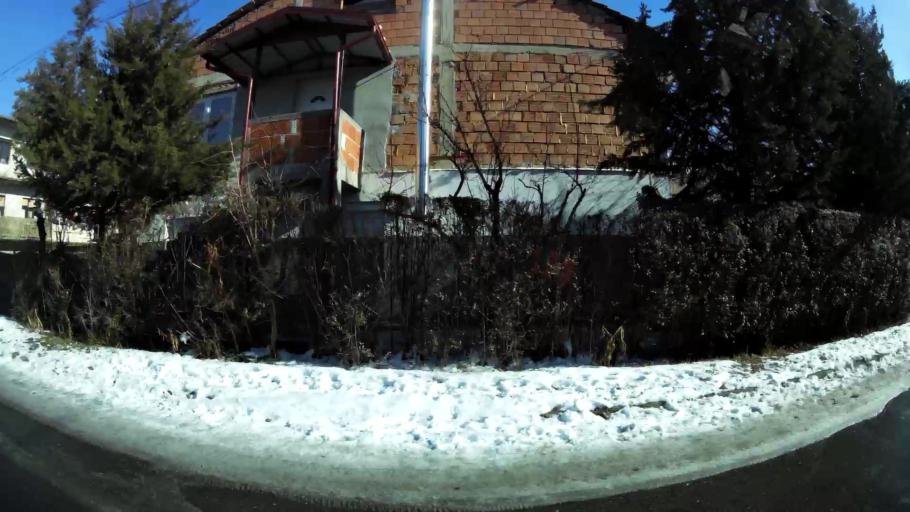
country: MK
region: Saraj
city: Saraj
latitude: 42.0095
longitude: 21.3506
